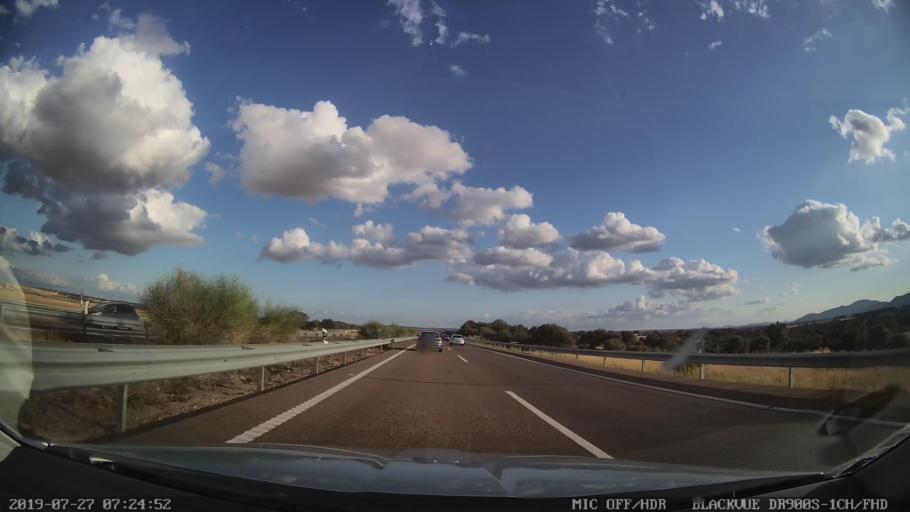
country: ES
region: Extremadura
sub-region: Provincia de Caceres
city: Puerto de Santa Cruz
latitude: 39.2883
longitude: -5.8547
